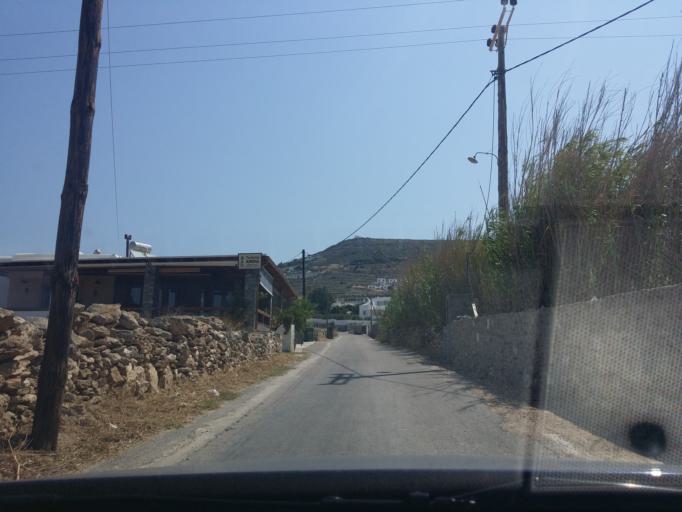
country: GR
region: South Aegean
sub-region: Nomos Kykladon
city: Antiparos
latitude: 37.0442
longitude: 25.1210
